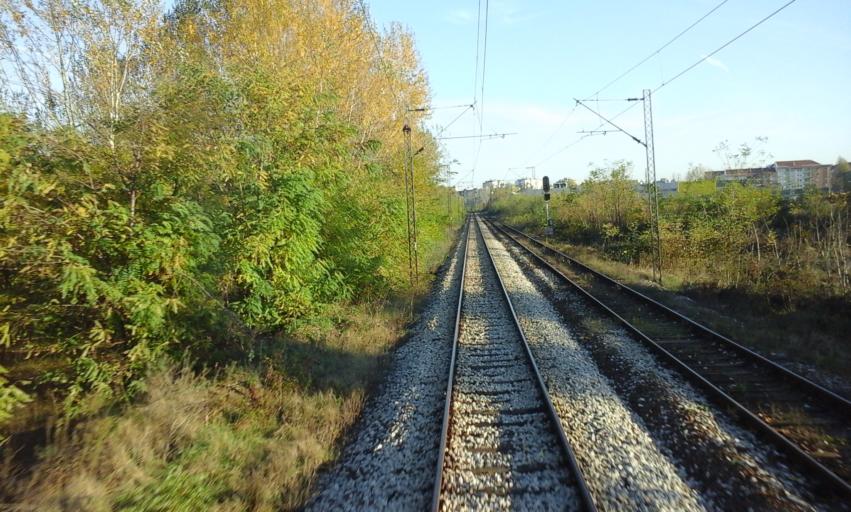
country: RS
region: Autonomna Pokrajina Vojvodina
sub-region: Juznobacki Okrug
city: Novi Sad
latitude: 45.2681
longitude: 19.8146
